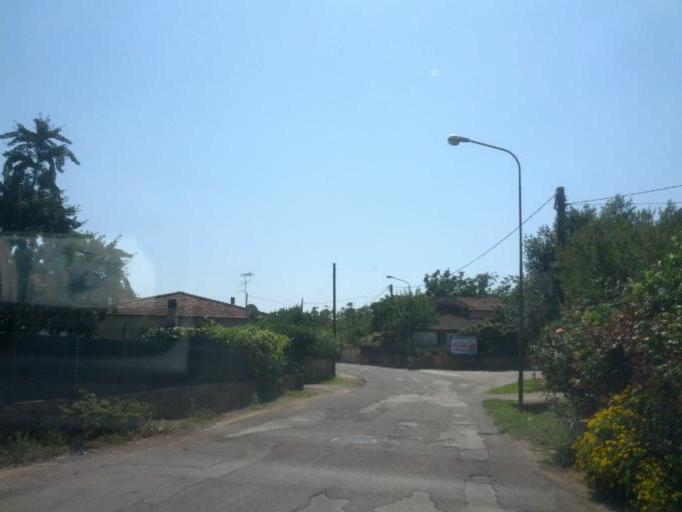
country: IT
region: Latium
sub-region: Provincia di Latina
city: Monte San Biagio
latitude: 41.3662
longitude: 13.3507
